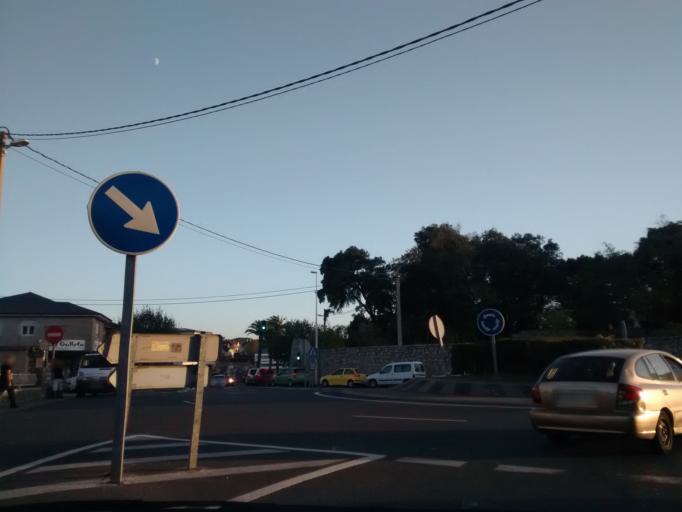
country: ES
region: Cantabria
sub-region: Provincia de Cantabria
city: Santa Cruz de Bezana
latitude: 43.4662
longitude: -3.8681
